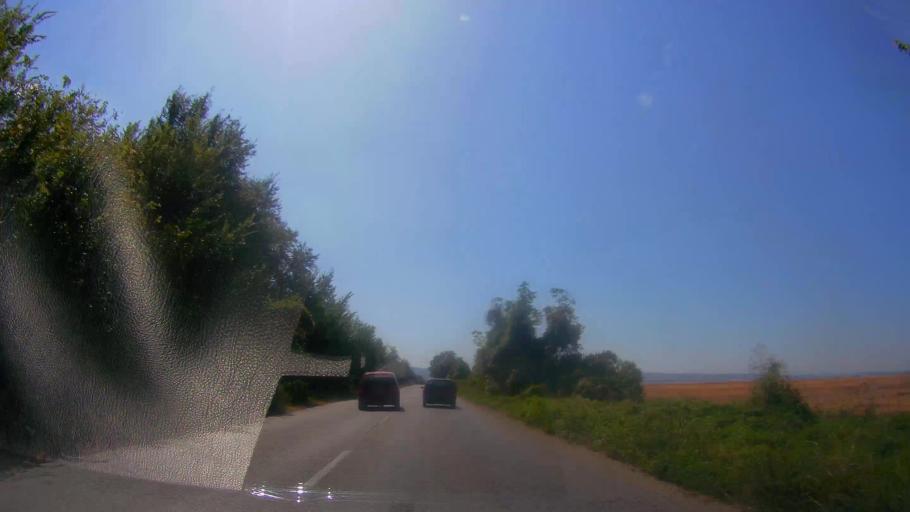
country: BG
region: Veliko Turnovo
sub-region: Obshtina Gorna Oryakhovitsa
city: Purvomaytsi
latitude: 43.2336
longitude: 25.6404
